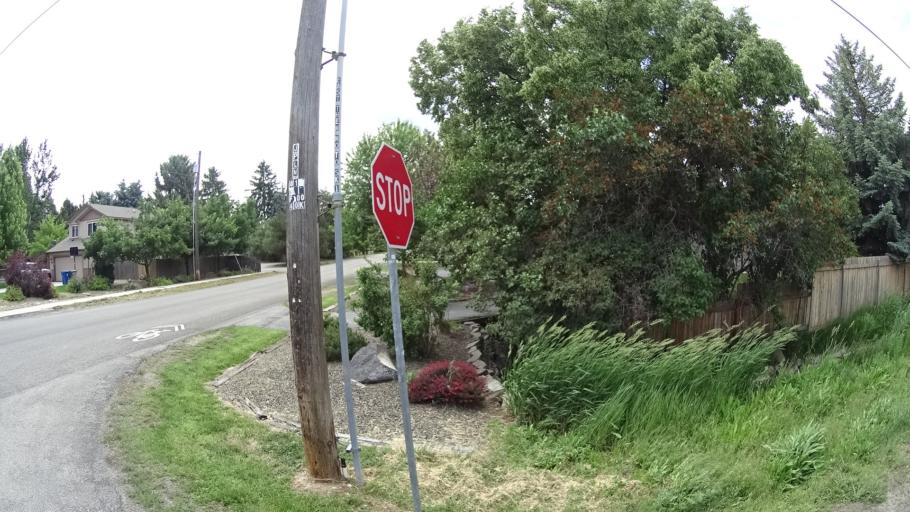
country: US
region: Idaho
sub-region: Ada County
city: Eagle
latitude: 43.6448
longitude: -116.3244
